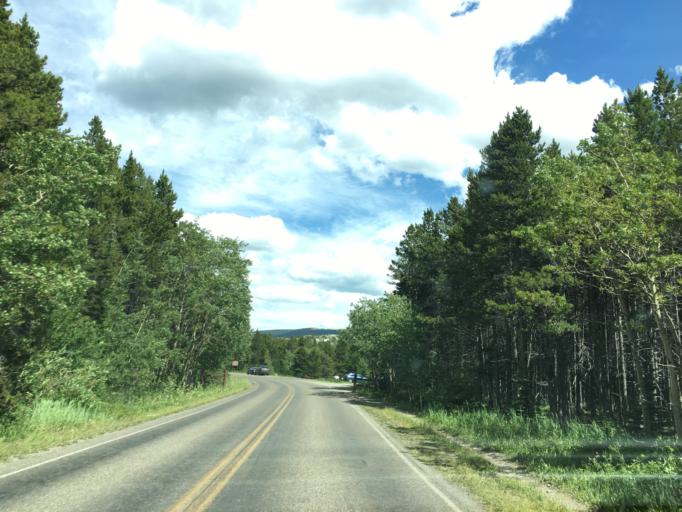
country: CA
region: Alberta
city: Cardston
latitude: 48.7977
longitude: -113.6703
